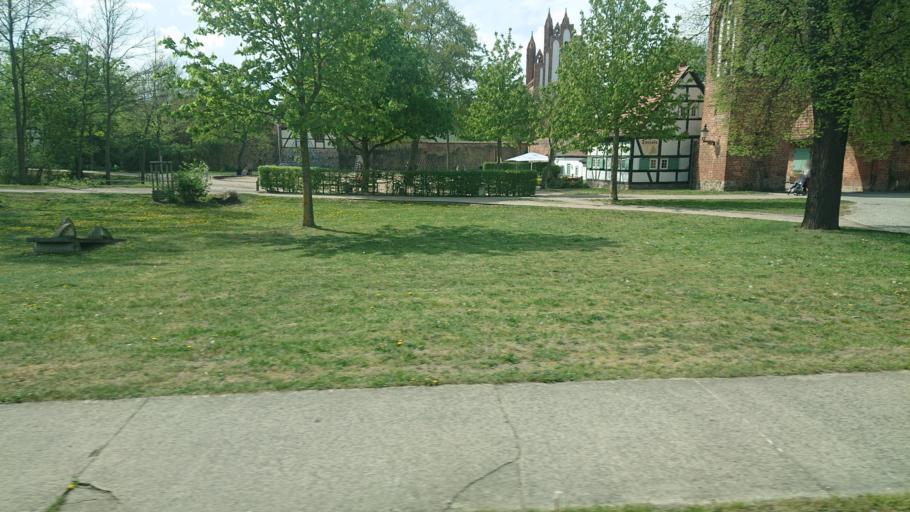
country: DE
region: Mecklenburg-Vorpommern
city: Neubrandenburg
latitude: 53.5590
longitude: 13.2664
